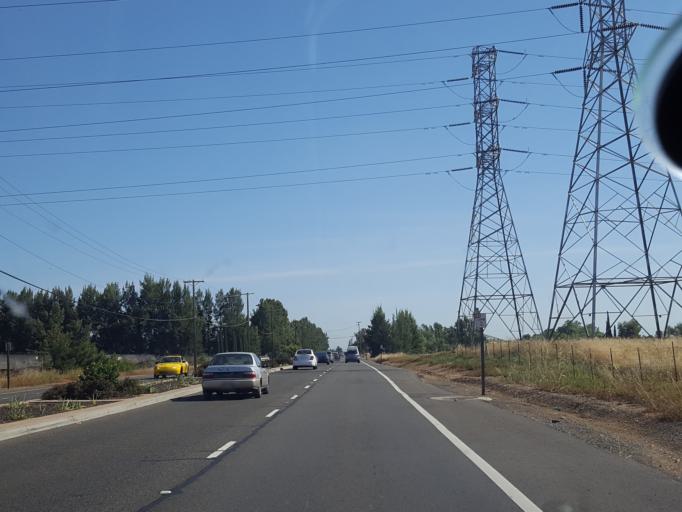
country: US
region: California
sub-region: Sacramento County
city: Vineyard
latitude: 38.5096
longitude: -121.3351
